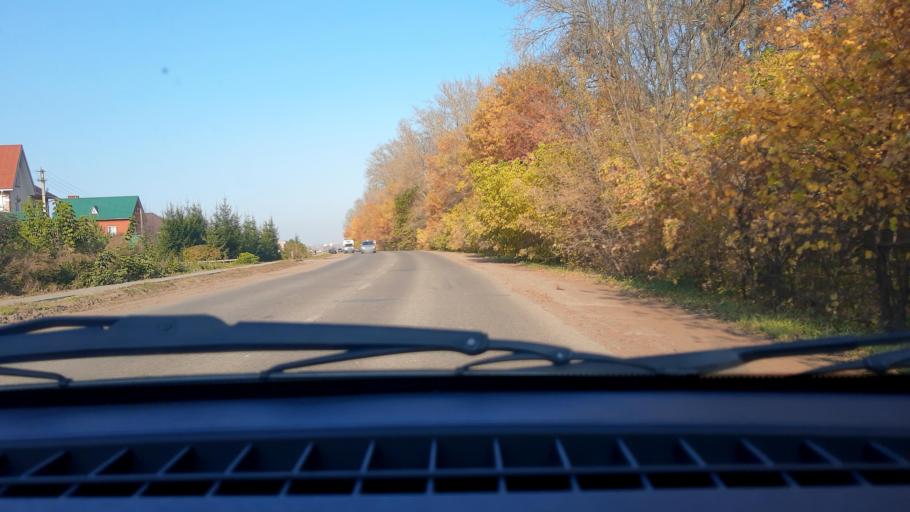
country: RU
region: Bashkortostan
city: Ufa
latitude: 54.7924
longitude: 55.9558
